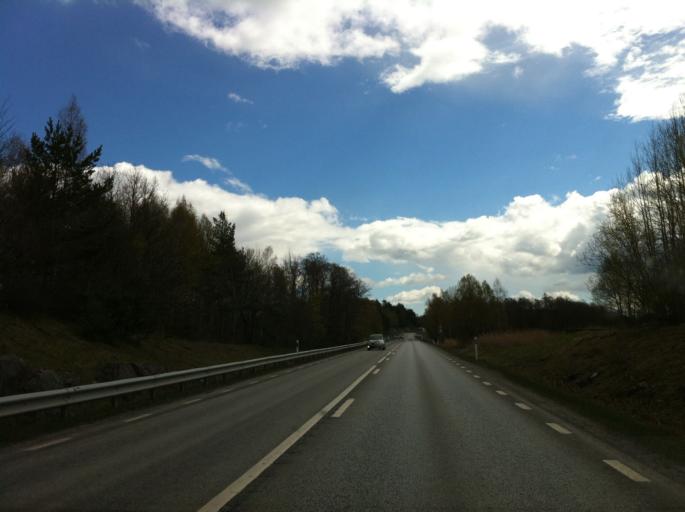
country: SE
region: Stockholm
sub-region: Vallentuna Kommun
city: Vallentuna
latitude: 59.4838
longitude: 18.1648
